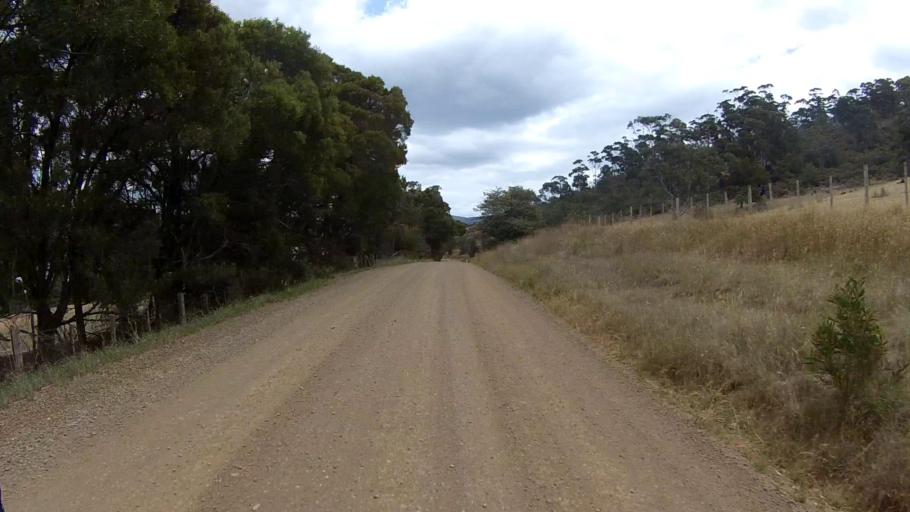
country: AU
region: Tasmania
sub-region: Sorell
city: Sorell
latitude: -42.6280
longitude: 147.9315
